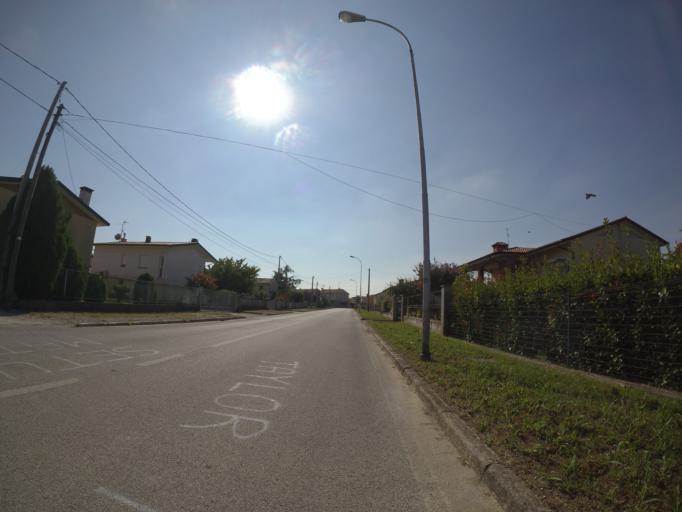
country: IT
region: Friuli Venezia Giulia
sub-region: Provincia di Udine
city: Muzzana del Turgnano
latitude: 45.8130
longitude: 13.1292
